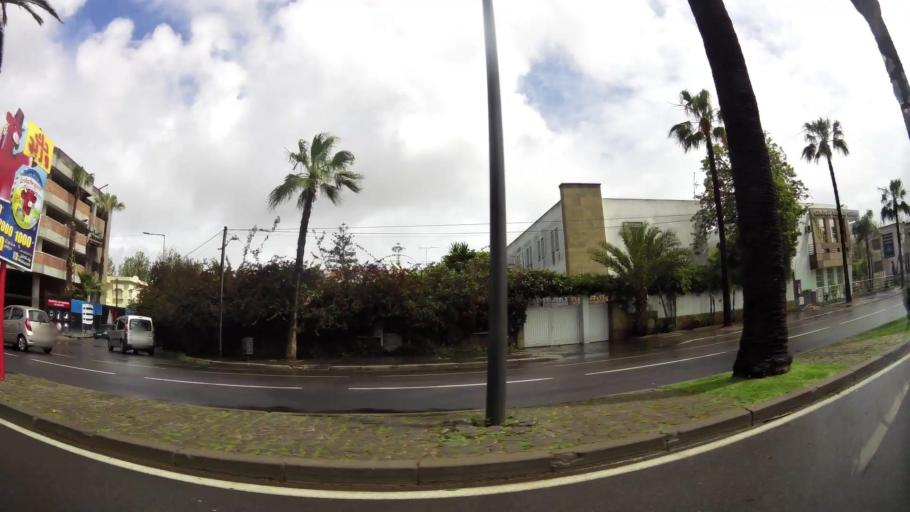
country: MA
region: Grand Casablanca
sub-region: Casablanca
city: Casablanca
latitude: 33.5683
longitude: -7.6424
